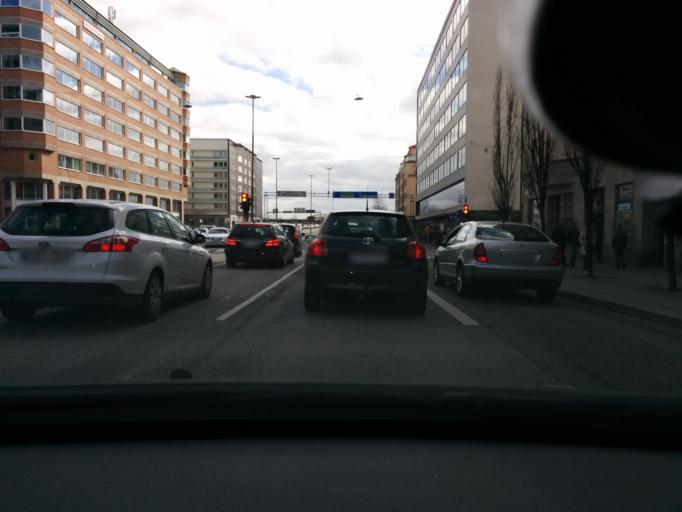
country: SE
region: Stockholm
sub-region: Stockholms Kommun
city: Arsta
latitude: 59.3164
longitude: 18.0333
